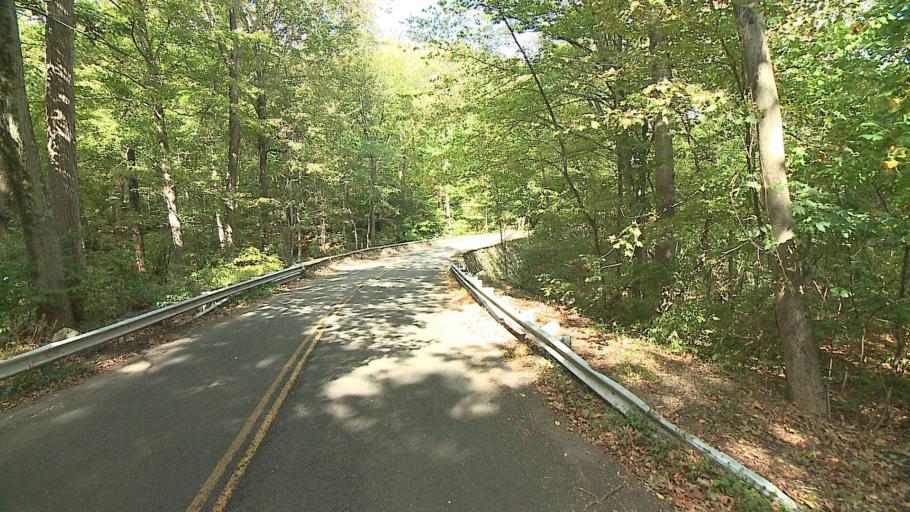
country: US
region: Connecticut
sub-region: Fairfield County
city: Shelton
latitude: 41.3385
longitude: -73.1243
